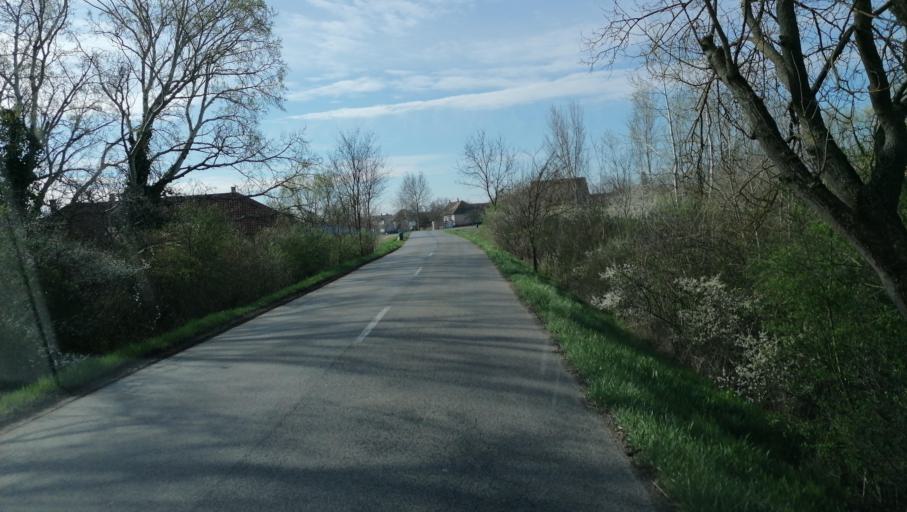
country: HU
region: Pest
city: Rackeve
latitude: 47.0970
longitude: 18.9273
